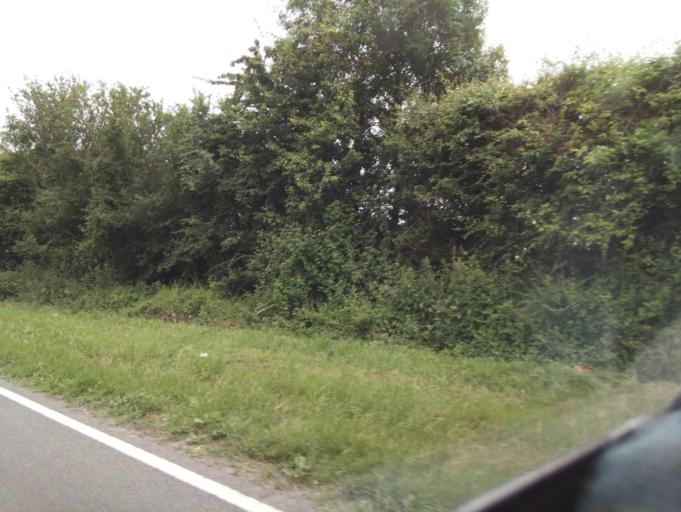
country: GB
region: England
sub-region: Leicestershire
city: Grimston
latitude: 52.7843
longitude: -1.0041
